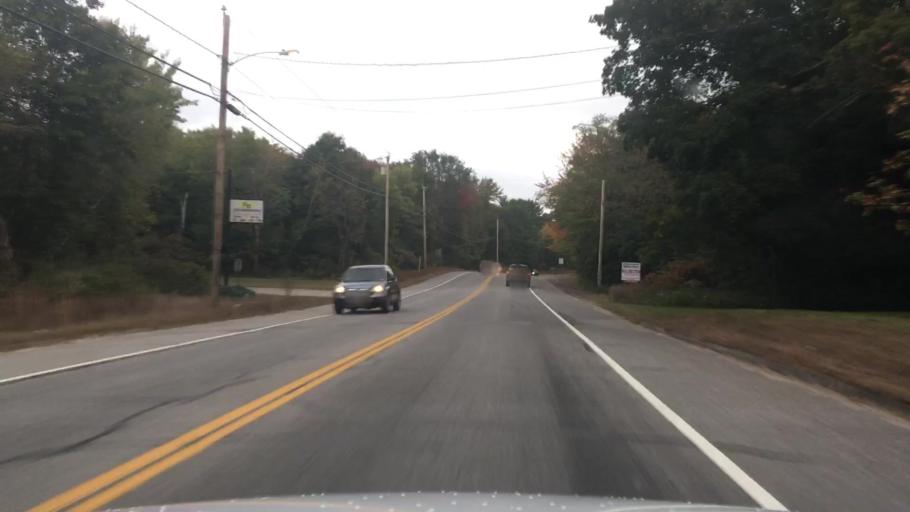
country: US
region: Maine
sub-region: York County
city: Waterboro
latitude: 43.5705
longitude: -70.6670
